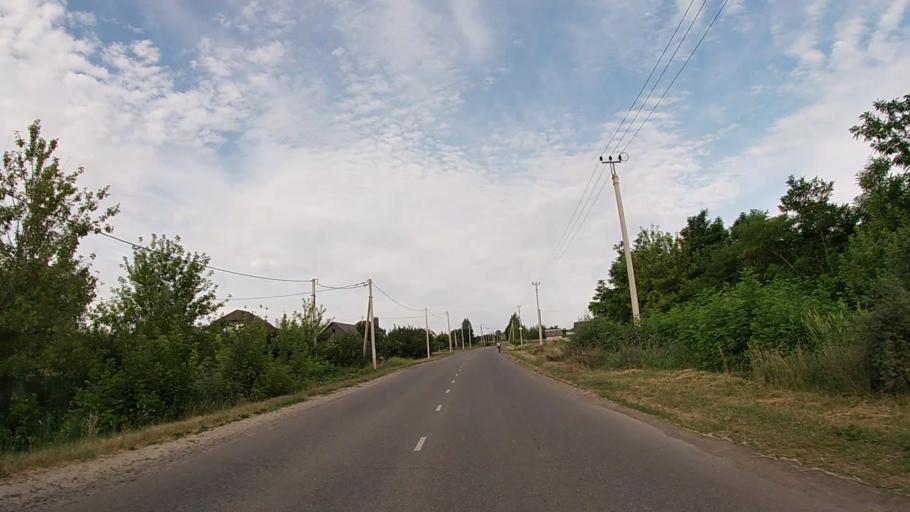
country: RU
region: Belgorod
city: Severnyy
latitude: 50.6945
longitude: 36.5704
